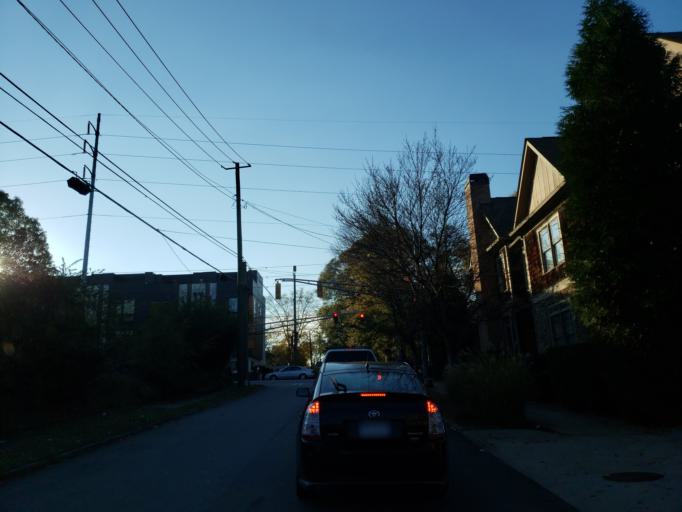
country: US
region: Georgia
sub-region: DeKalb County
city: Druid Hills
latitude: 33.7554
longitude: -84.3487
